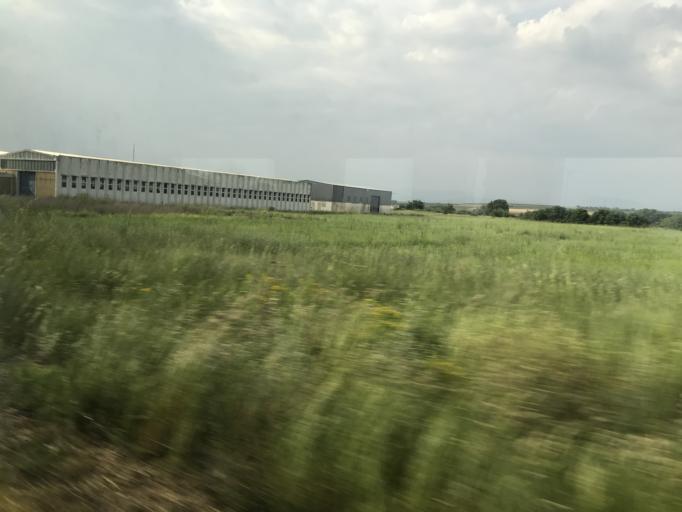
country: GR
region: East Macedonia and Thrace
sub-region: Nomos Rodopis
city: Lykeio
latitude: 41.0406
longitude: 25.6609
